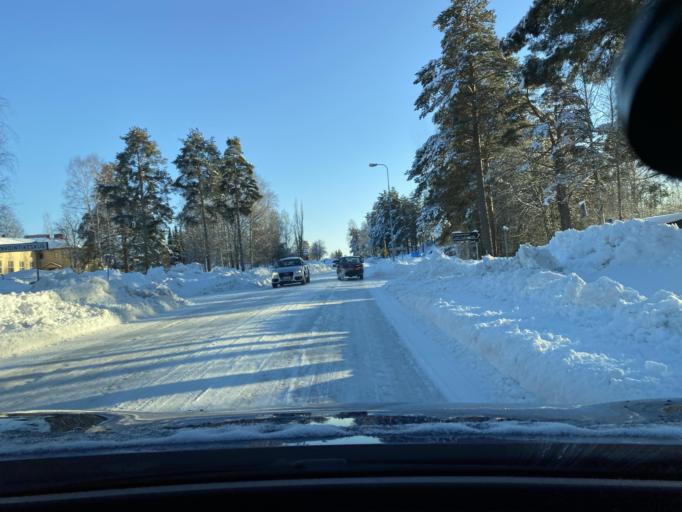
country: FI
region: Southern Savonia
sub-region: Mikkeli
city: Kangasniemi
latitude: 61.9920
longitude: 26.6340
